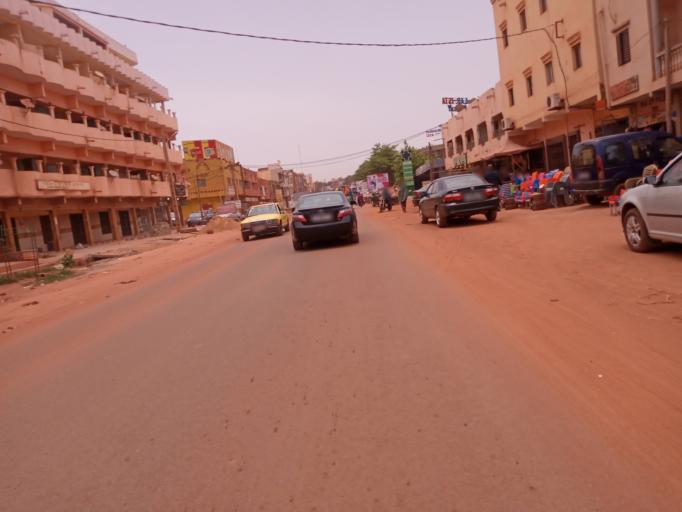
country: ML
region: Bamako
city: Bamako
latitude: 12.5763
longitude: -8.0112
